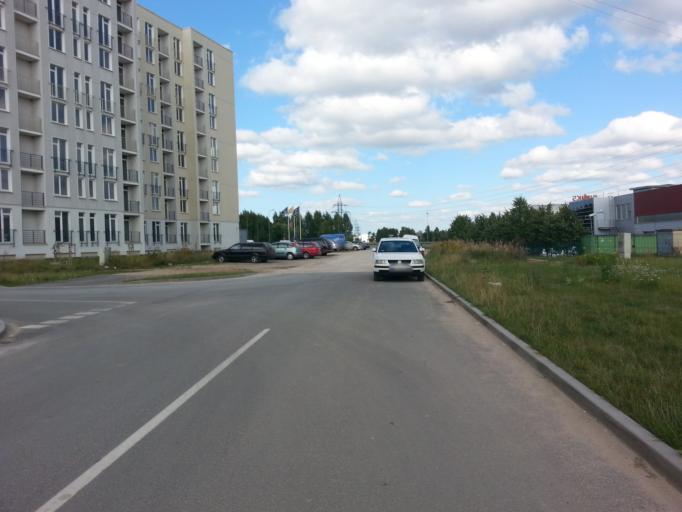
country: LV
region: Stopini
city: Ulbroka
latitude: 56.9417
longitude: 24.2307
